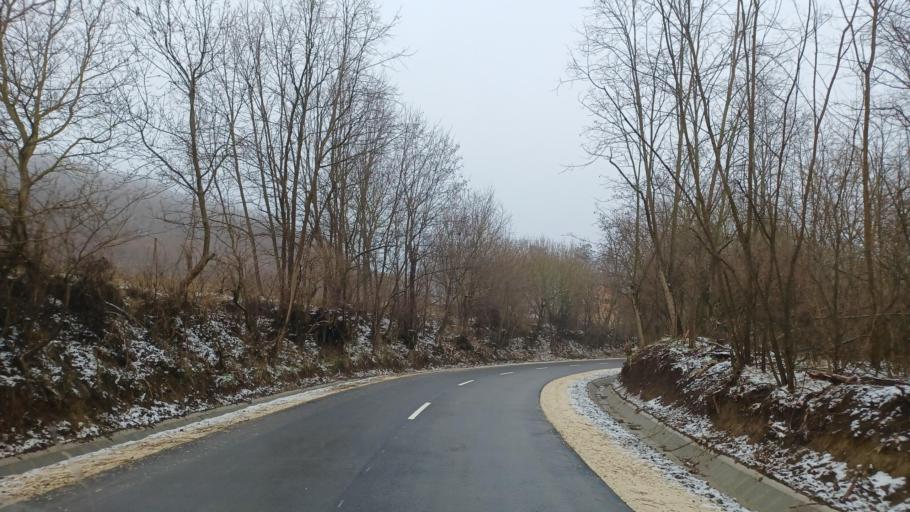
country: HU
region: Tolna
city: Gyonk
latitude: 46.5994
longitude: 18.4735
